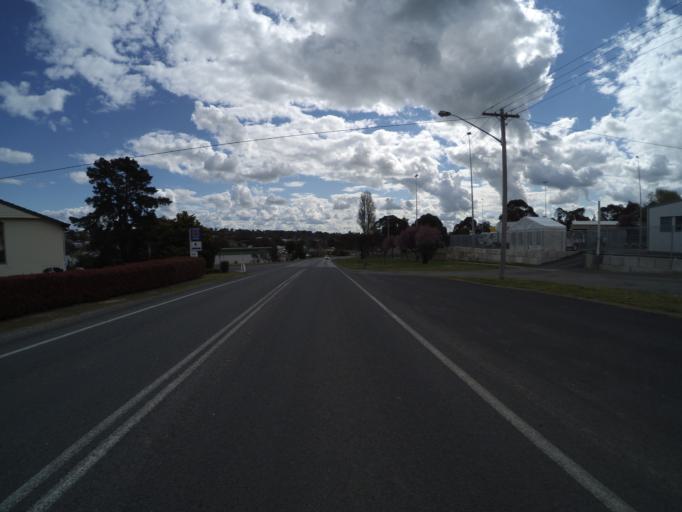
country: AU
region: New South Wales
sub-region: Yass Valley
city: Yass
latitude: -34.8504
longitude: 148.9198
